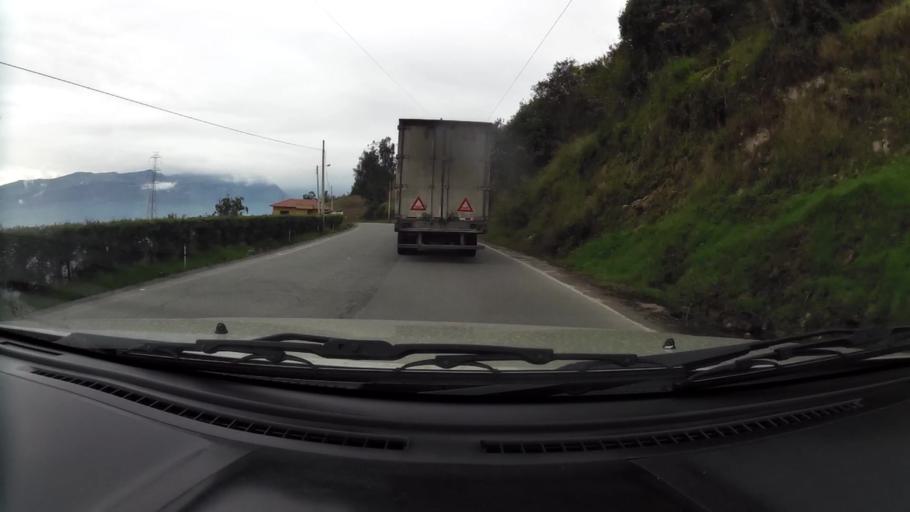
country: EC
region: Chimborazo
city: Alausi
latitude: -2.3093
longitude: -78.9277
